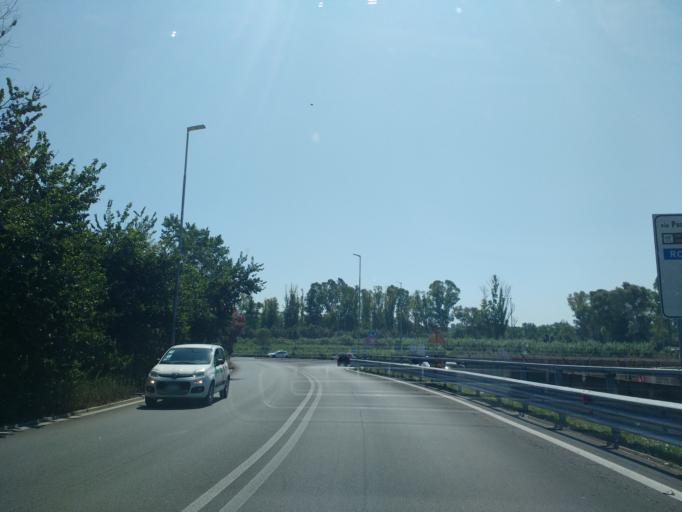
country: IT
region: Latium
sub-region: Citta metropolitana di Roma Capitale
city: Fiumicino-Isola Sacra
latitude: 41.7822
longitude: 12.2534
